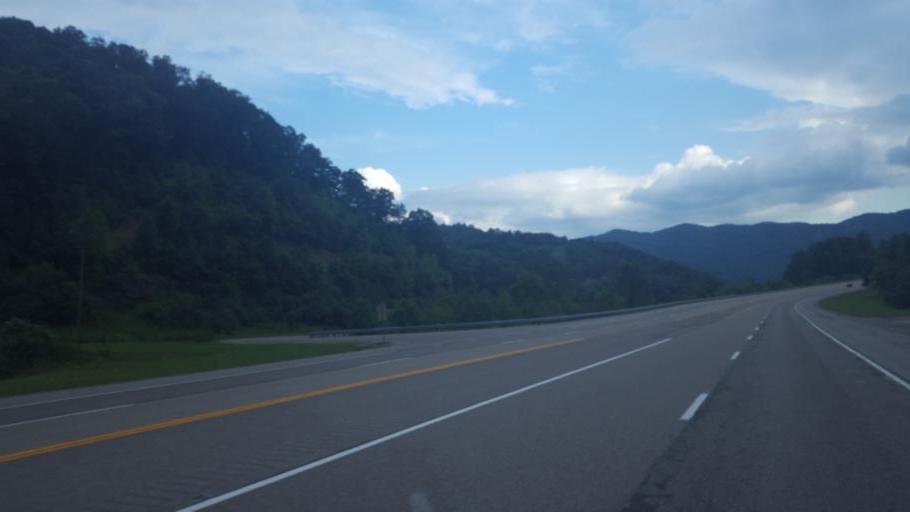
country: US
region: Kentucky
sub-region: Letcher County
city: Jenkins
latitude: 37.2040
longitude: -82.6231
